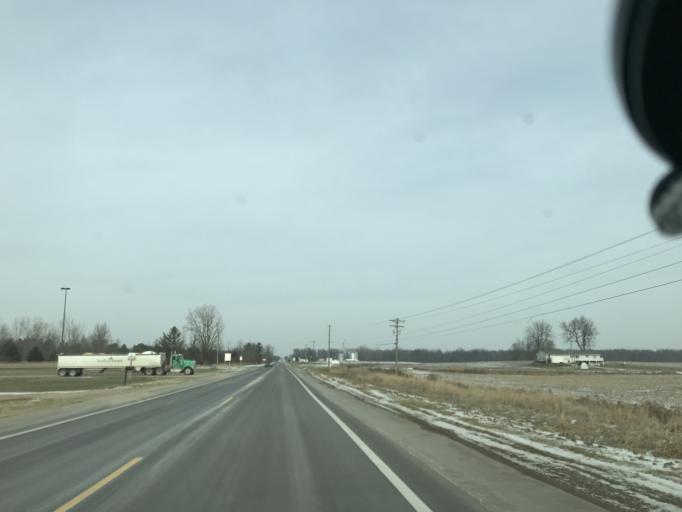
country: US
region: Michigan
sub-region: Ionia County
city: Lake Odessa
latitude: 42.7981
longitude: -85.0745
